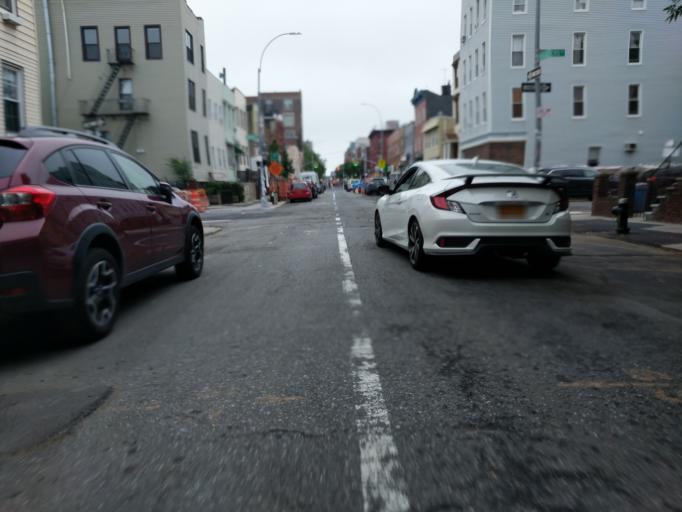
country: US
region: New York
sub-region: Queens County
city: Long Island City
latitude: 40.7123
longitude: -73.9474
